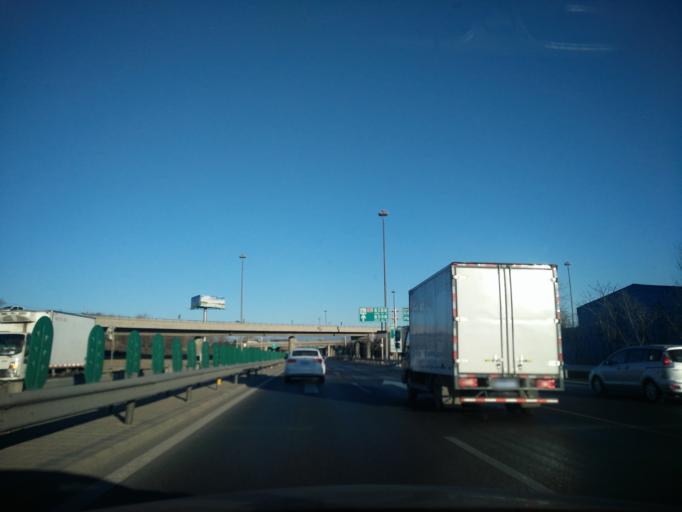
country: CN
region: Beijing
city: Fengtai
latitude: 39.8417
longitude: 116.2214
